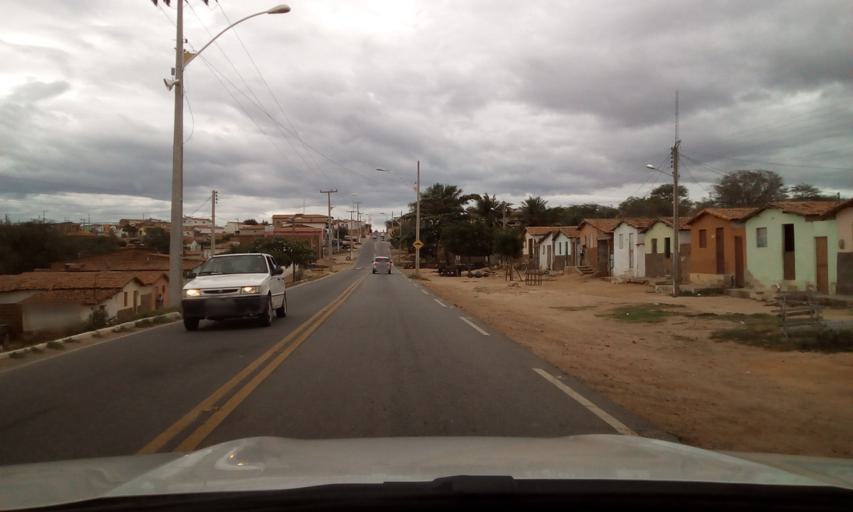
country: BR
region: Paraiba
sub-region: Picui
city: Picui
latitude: -6.5130
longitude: -36.3369
